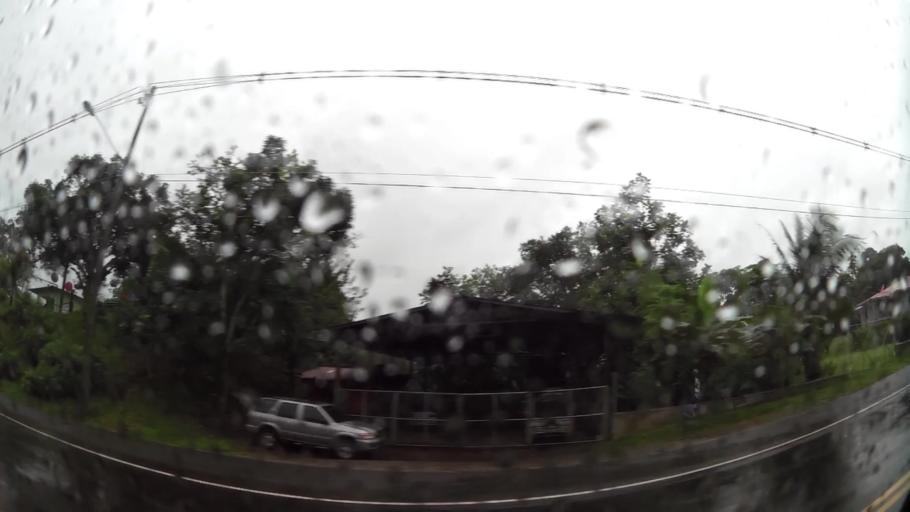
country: PA
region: Colon
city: Quebrada Bonita Adentro
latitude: 9.2862
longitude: -79.7224
